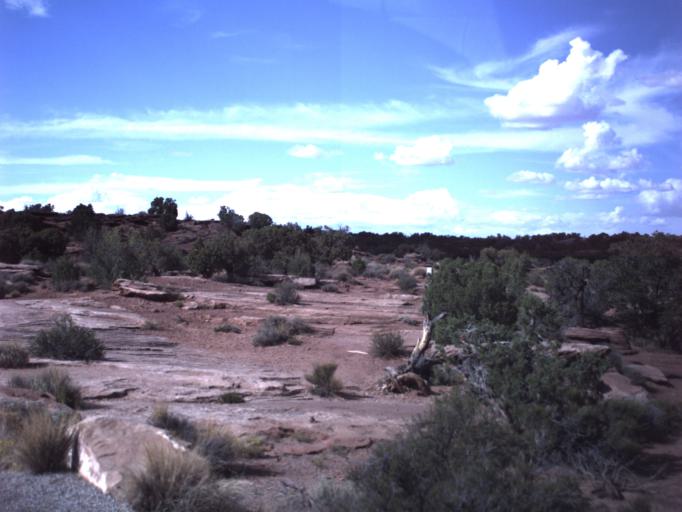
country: US
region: Utah
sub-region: Grand County
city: Moab
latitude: 38.4749
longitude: -109.7410
